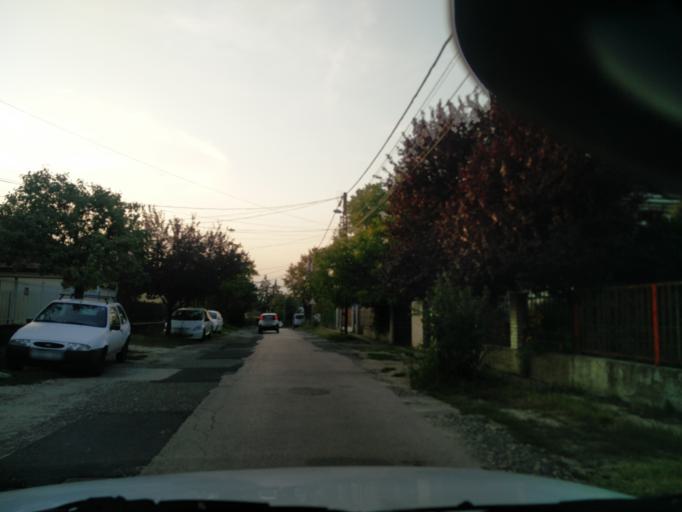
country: HU
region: Budapest
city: Budapest XXIII. keruelet
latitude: 47.4040
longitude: 19.0883
